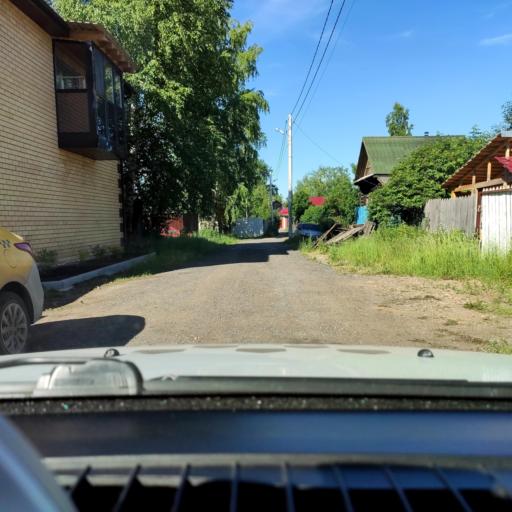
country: RU
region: Perm
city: Perm
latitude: 58.0334
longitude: 56.2398
